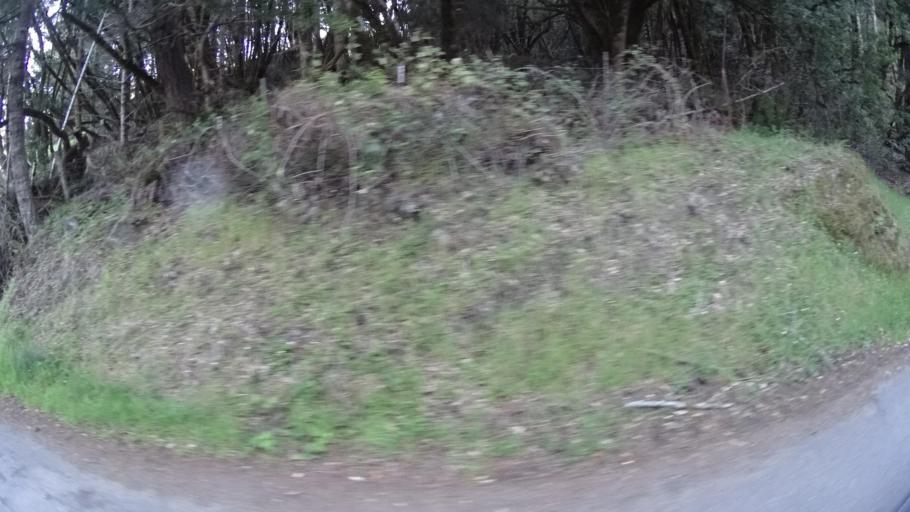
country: US
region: California
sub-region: Humboldt County
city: Hydesville
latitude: 40.6551
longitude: -123.9236
